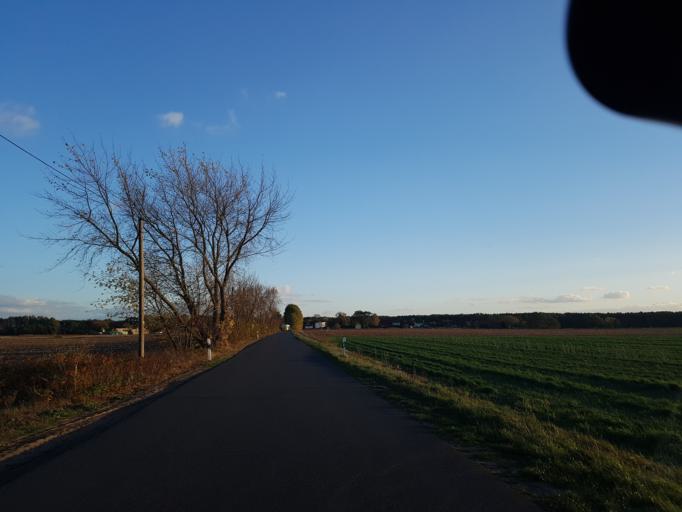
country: DE
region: Brandenburg
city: Beelitz
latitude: 52.1900
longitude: 12.9241
